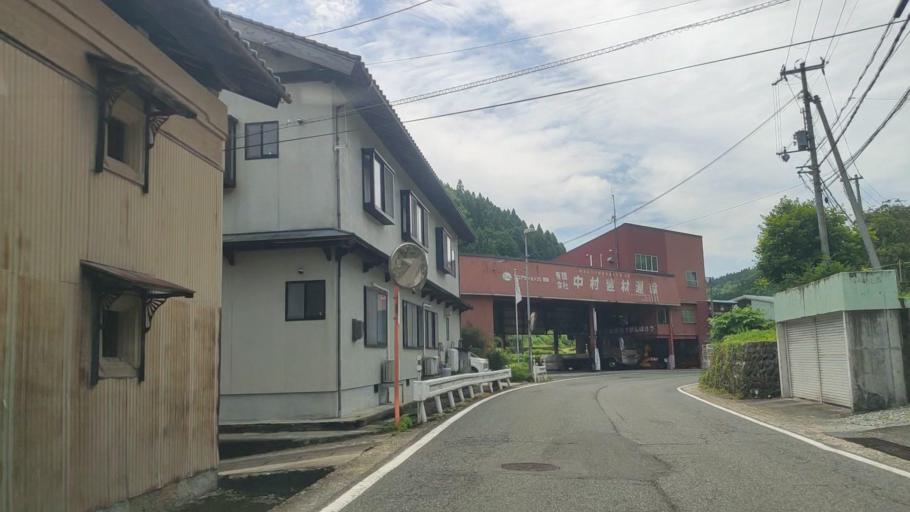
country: JP
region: Hyogo
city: Toyooka
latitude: 35.4846
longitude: 134.5533
